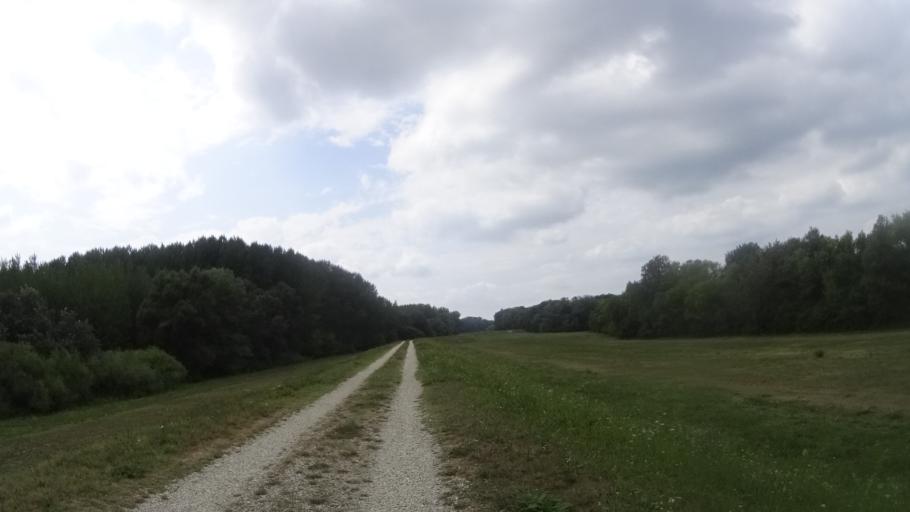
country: SK
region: Trnavsky
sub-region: Okres Dunajska Streda
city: Velky Meder
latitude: 47.7567
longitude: 17.7536
